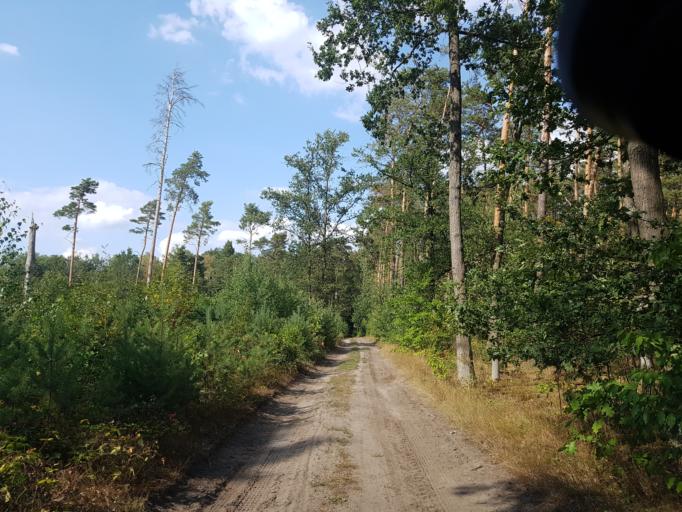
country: DE
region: Brandenburg
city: Calau
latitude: 51.7648
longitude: 13.9520
